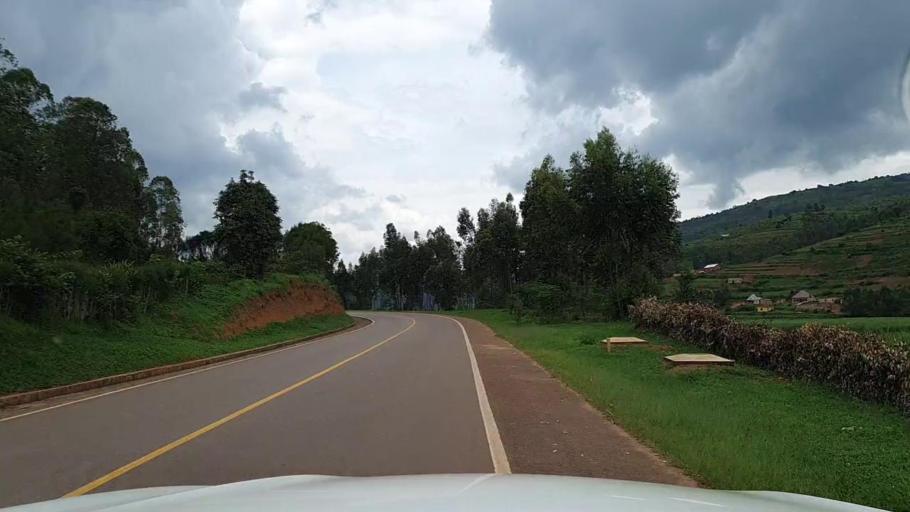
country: RW
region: Kigali
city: Kigali
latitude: -1.7764
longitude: 30.1274
